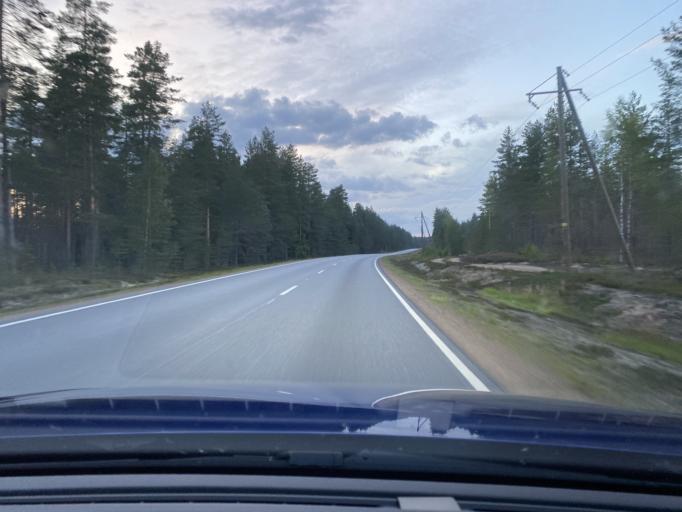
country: FI
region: Satakunta
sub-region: Pohjois-Satakunta
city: Honkajoki
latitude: 62.2021
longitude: 22.2996
